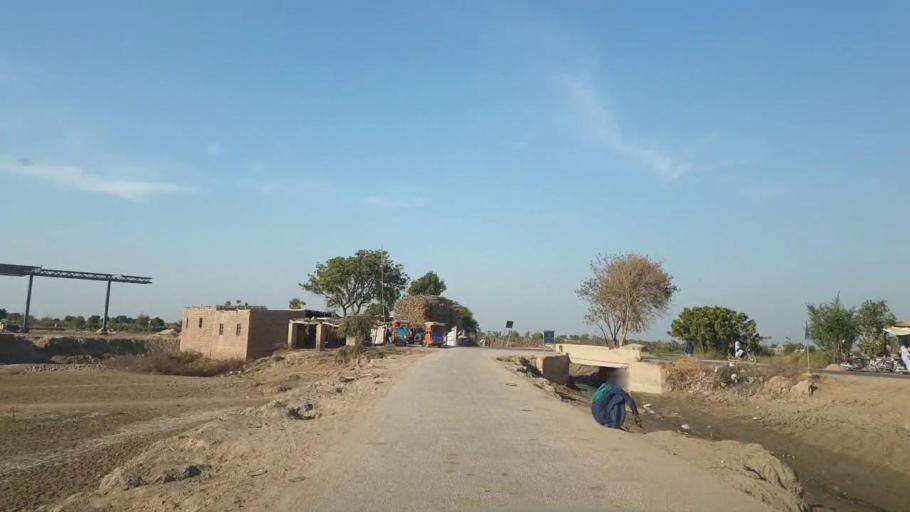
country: PK
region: Sindh
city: Tando Adam
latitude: 25.7307
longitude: 68.7024
